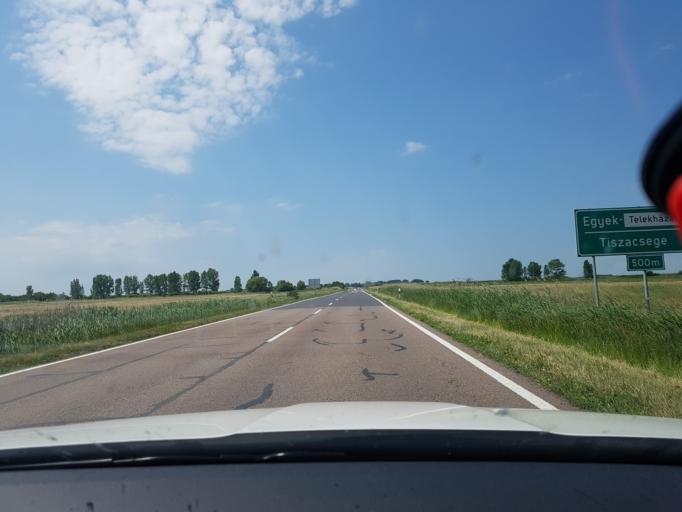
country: HU
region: Hajdu-Bihar
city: Tiszacsege
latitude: 47.5888
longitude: 21.0341
